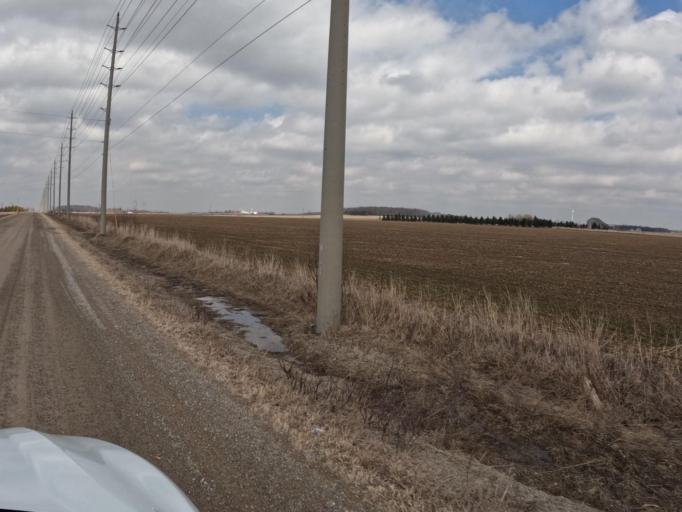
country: CA
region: Ontario
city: Shelburne
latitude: 44.0419
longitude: -80.3178
